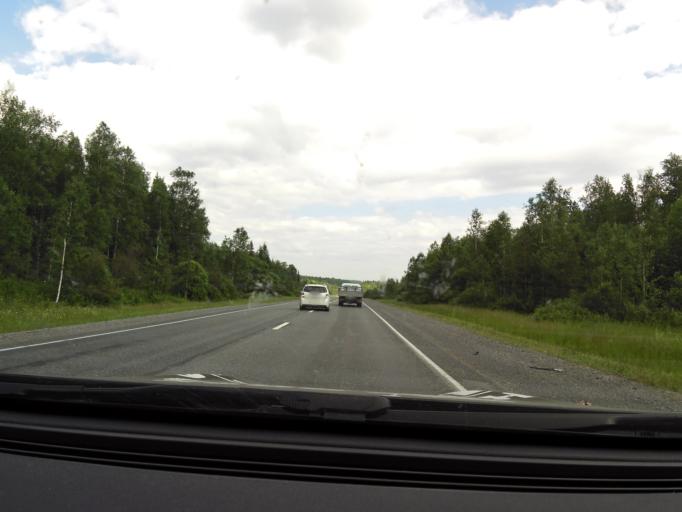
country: RU
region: Sverdlovsk
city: Nizhniye Sergi
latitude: 56.8249
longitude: 59.2516
